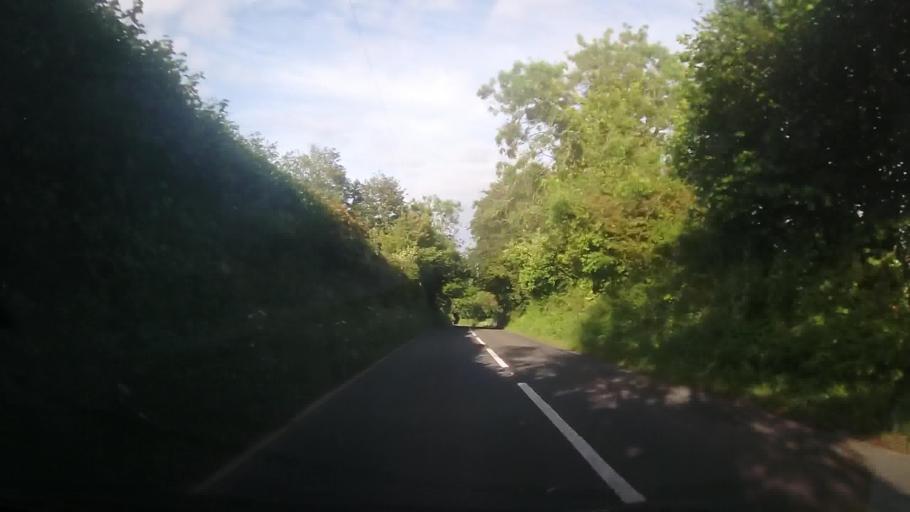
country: GB
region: England
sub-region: Devon
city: Ivybridge
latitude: 50.3517
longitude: -3.9420
